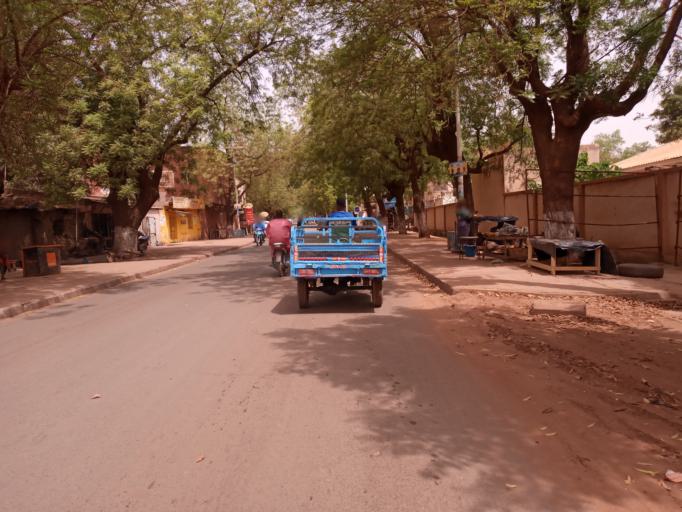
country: ML
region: Bamako
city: Bamako
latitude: 12.6505
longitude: -7.9808
